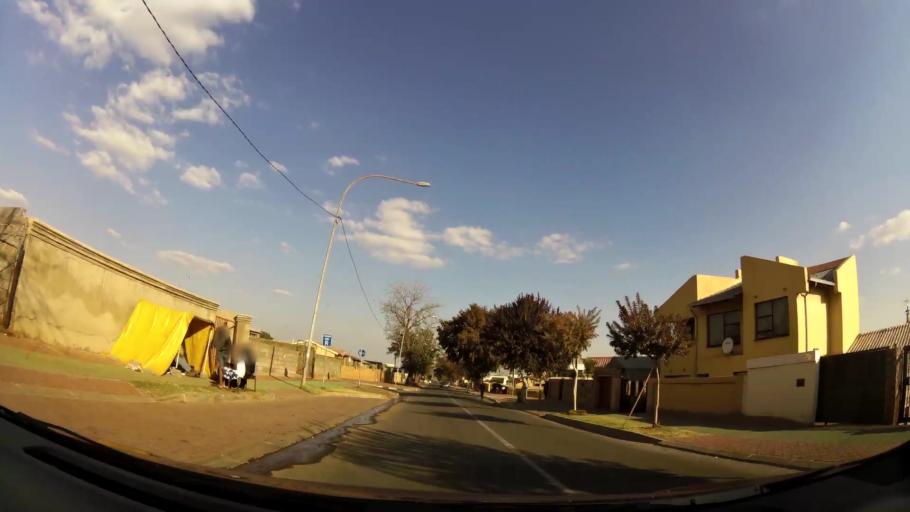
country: ZA
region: Gauteng
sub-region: City of Johannesburg Metropolitan Municipality
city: Roodepoort
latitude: -26.2079
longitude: 27.8843
